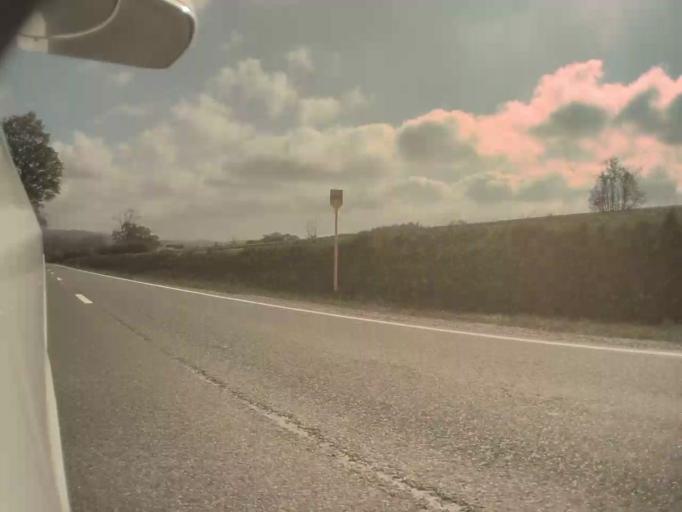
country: BE
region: Wallonia
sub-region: Province de Namur
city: Somme-Leuze
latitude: 50.3268
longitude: 5.3549
